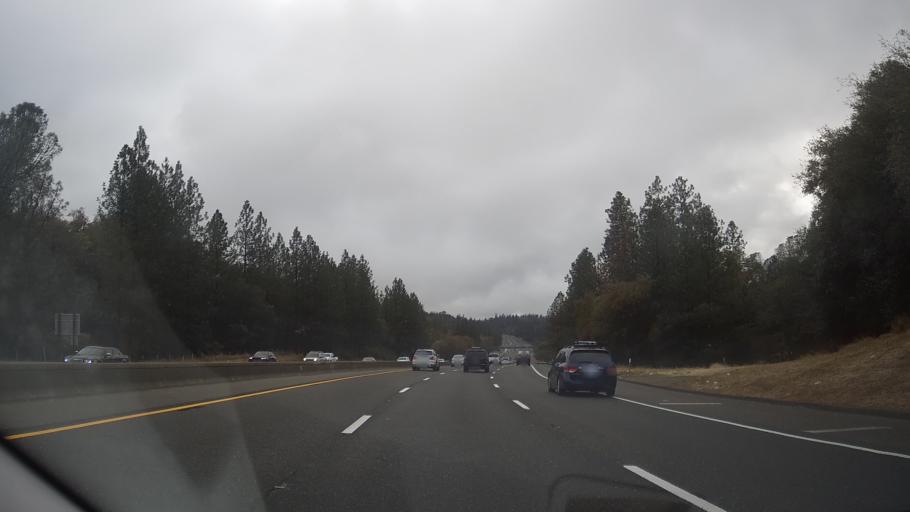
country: US
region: California
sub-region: Placer County
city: Meadow Vista
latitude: 38.9644
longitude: -121.0224
